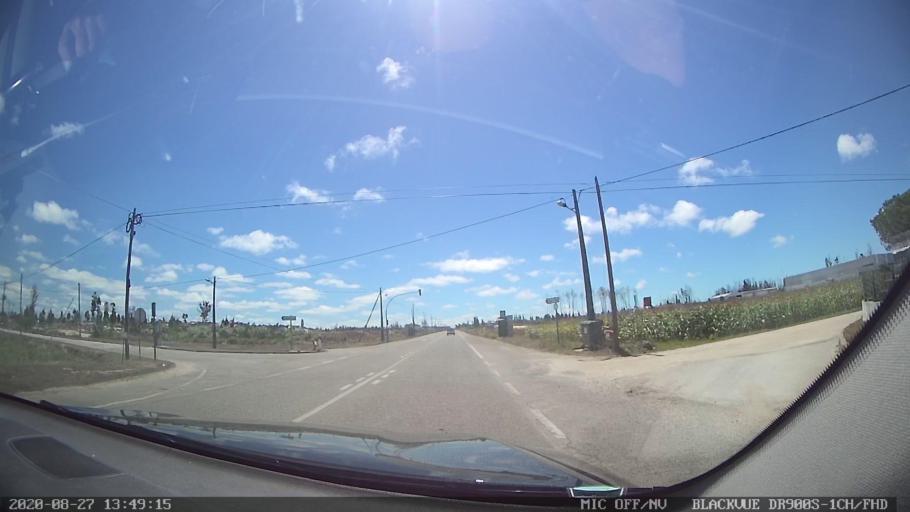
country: PT
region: Coimbra
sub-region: Mira
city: Mira
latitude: 40.3693
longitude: -8.7459
